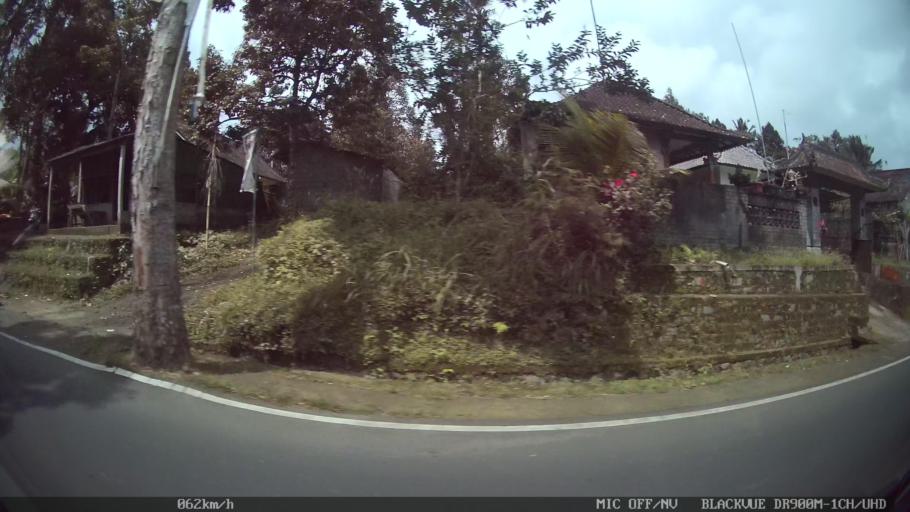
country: ID
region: Bali
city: Banjar Kubu
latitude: -8.4010
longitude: 115.4206
